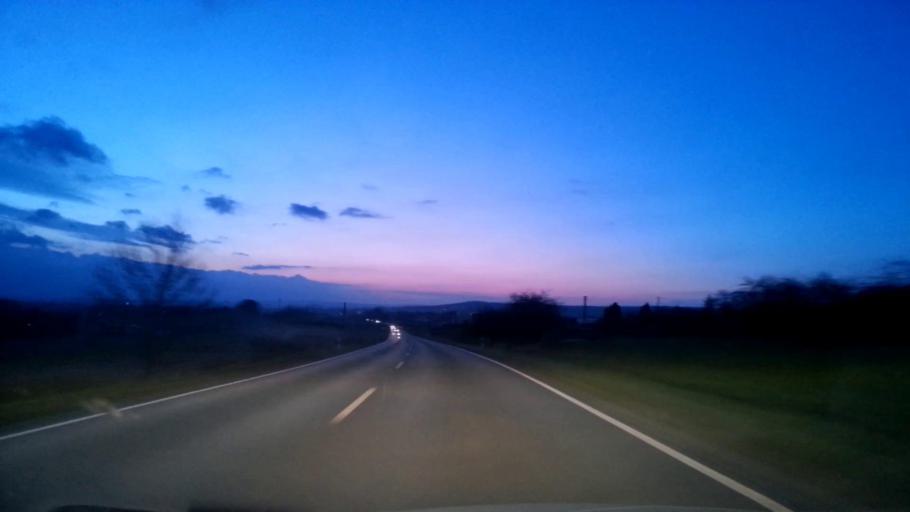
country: DE
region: Bavaria
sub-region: Upper Franconia
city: Bindlach
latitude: 49.9632
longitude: 11.6362
